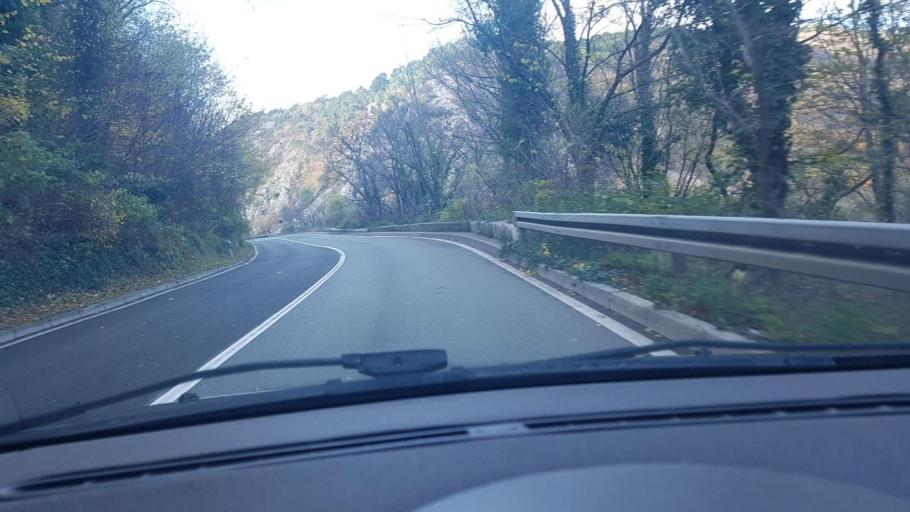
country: HR
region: Primorsko-Goranska
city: Cavle
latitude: 45.3365
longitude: 14.4662
